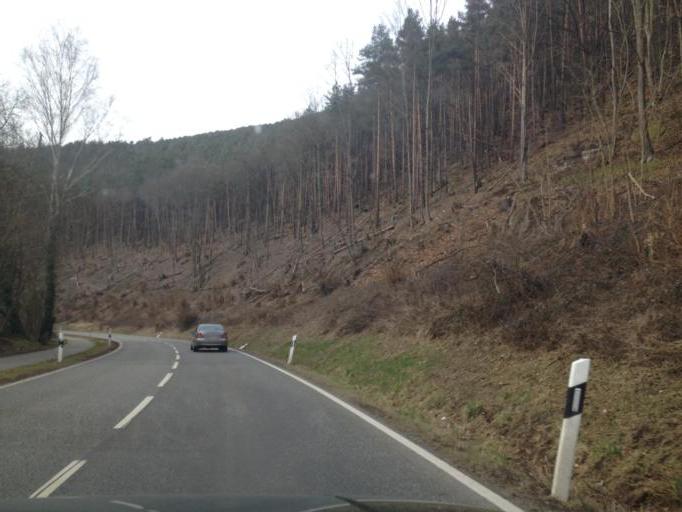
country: DE
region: Rheinland-Pfalz
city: Bad Duerkheim
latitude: 49.4649
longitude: 8.1184
